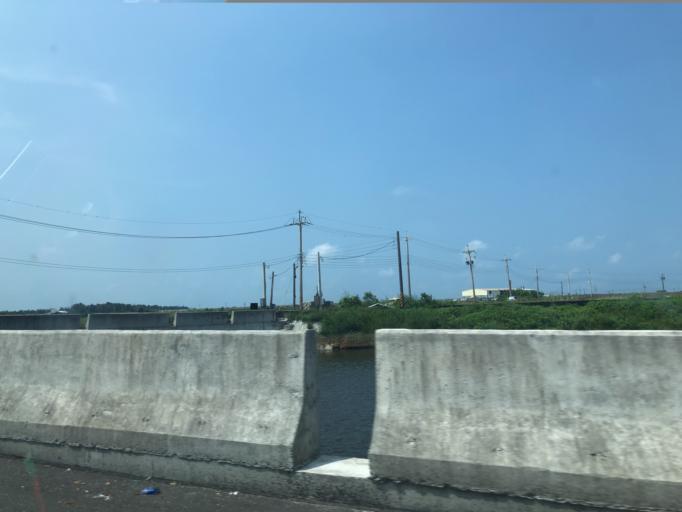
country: TW
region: Taiwan
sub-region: Chiayi
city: Taibao
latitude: 23.4637
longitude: 120.1510
